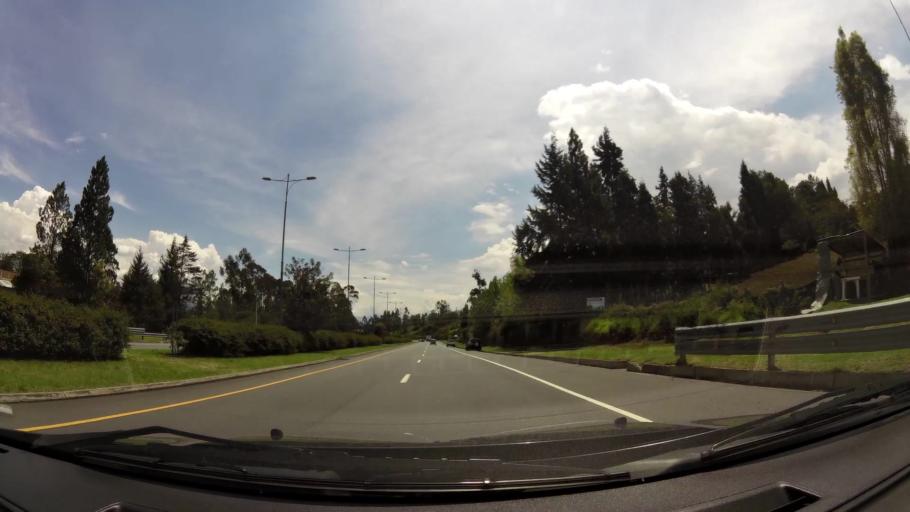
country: EC
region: Pichincha
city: Sangolqui
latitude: -0.1852
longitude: -78.3393
